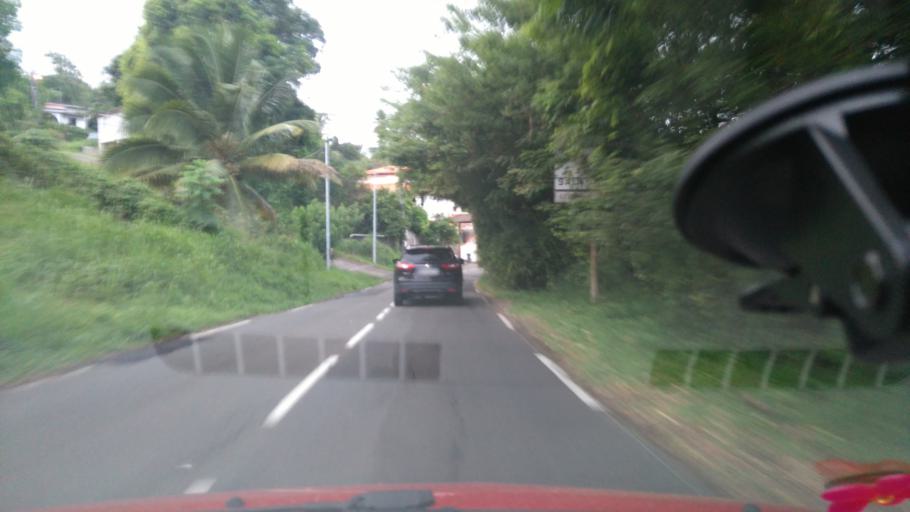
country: MQ
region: Martinique
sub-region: Martinique
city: Saint-Esprit
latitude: 14.5547
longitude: -60.9541
